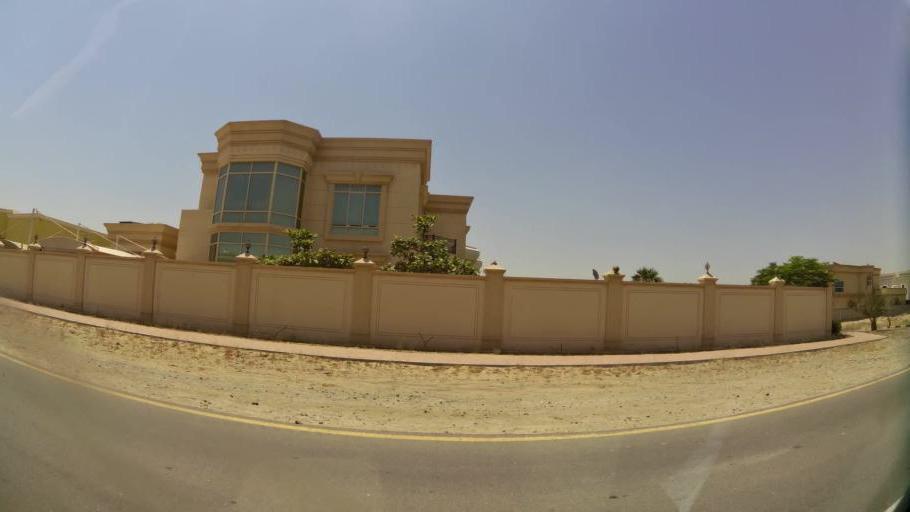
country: AE
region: Ajman
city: Ajman
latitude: 25.4256
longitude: 55.5144
